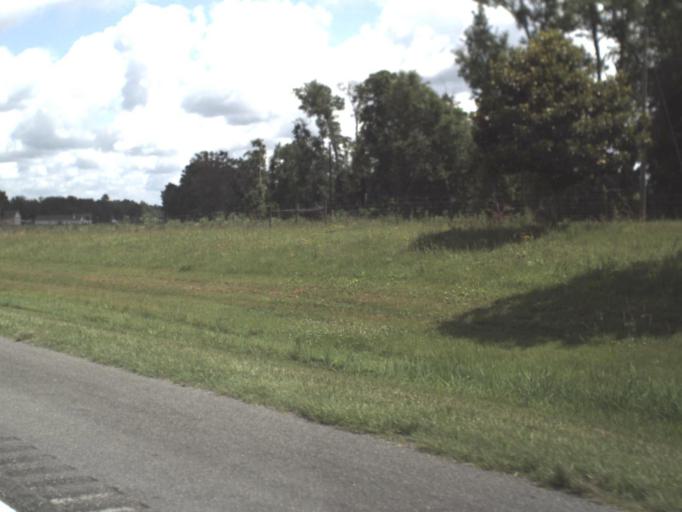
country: US
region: Florida
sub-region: Columbia County
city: Lake City
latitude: 30.1408
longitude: -82.6685
